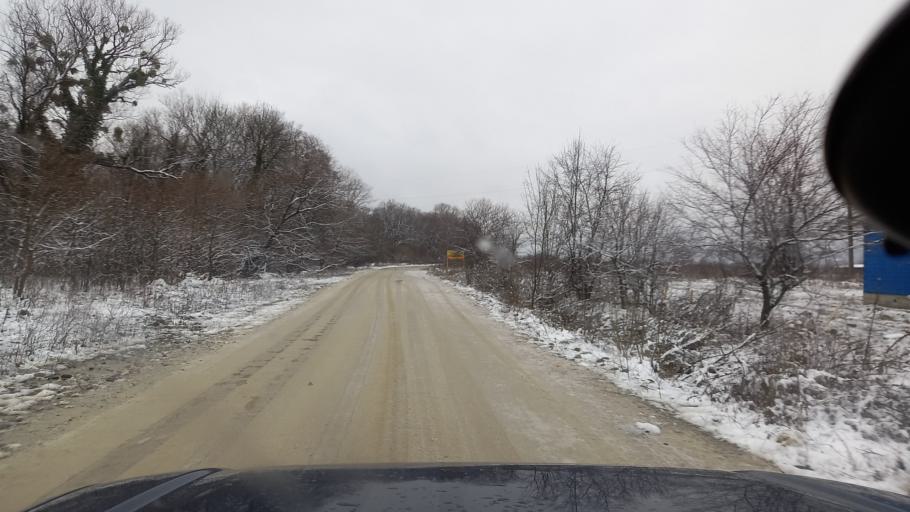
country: RU
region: Adygeya
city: Kamennomostskiy
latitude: 44.2302
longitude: 40.1866
